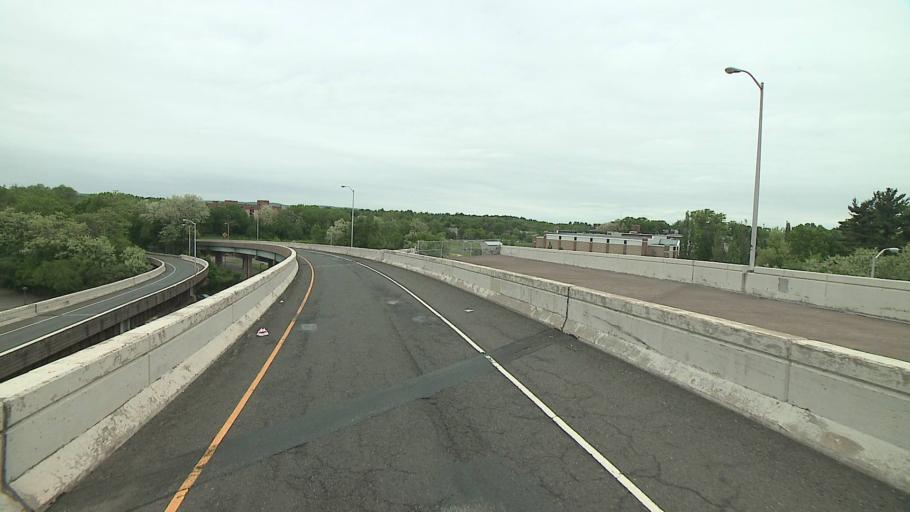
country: US
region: Connecticut
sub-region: Hartford County
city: Hartford
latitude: 41.7619
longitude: -72.7006
